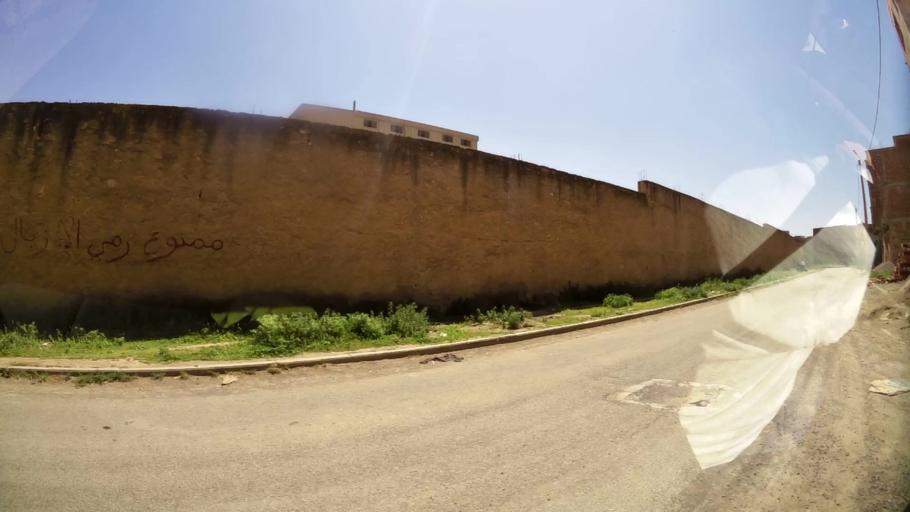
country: MA
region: Oriental
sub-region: Oujda-Angad
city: Oujda
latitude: 34.6897
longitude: -1.9367
